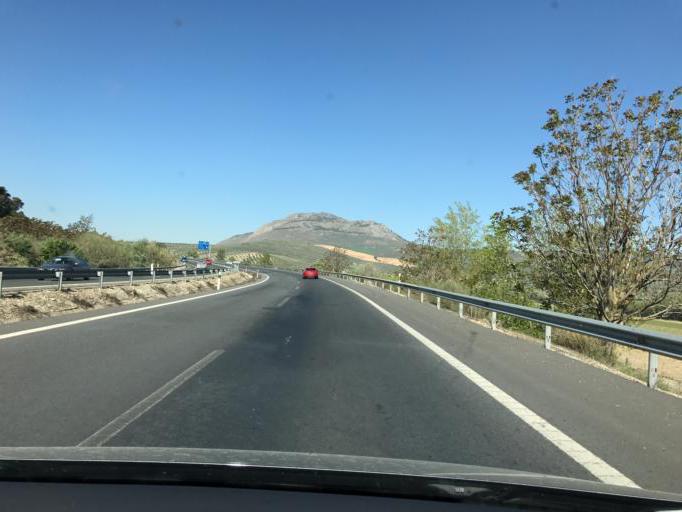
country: ES
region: Andalusia
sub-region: Provincia de Granada
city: Salar
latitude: 37.1810
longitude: -4.0744
